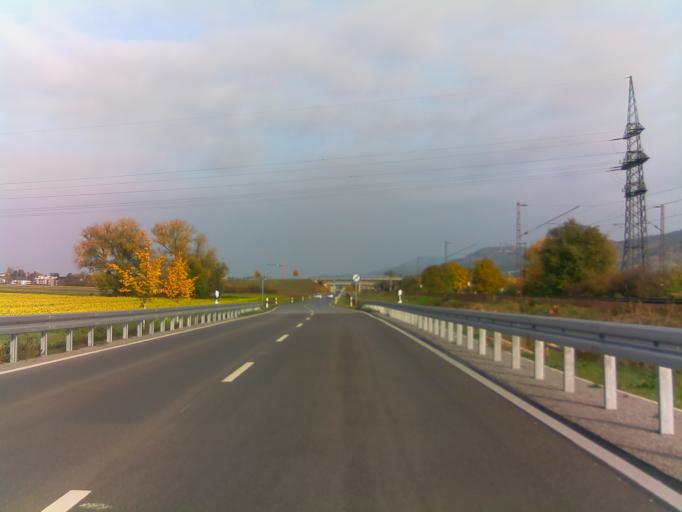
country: DE
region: Baden-Wuerttemberg
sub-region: Karlsruhe Region
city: Hemsbach
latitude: 49.5977
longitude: 8.6471
